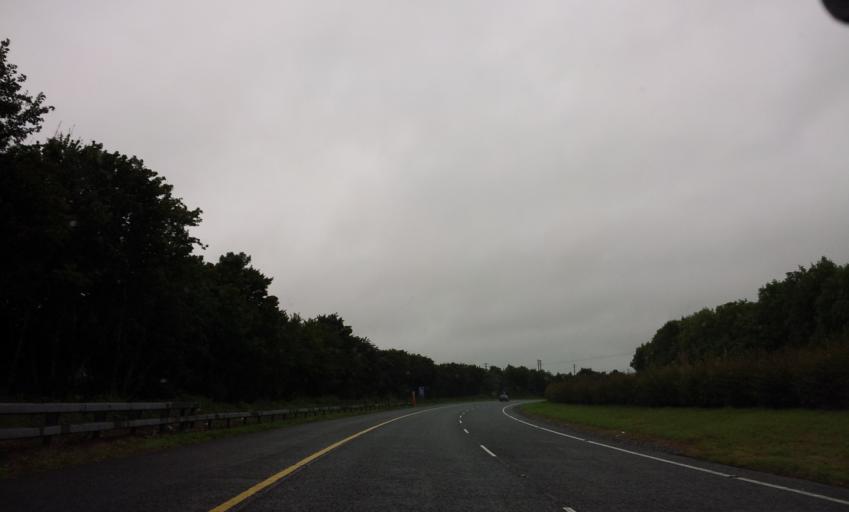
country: IE
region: Munster
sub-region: County Cork
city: Watergrasshill
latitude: 51.9429
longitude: -8.3925
